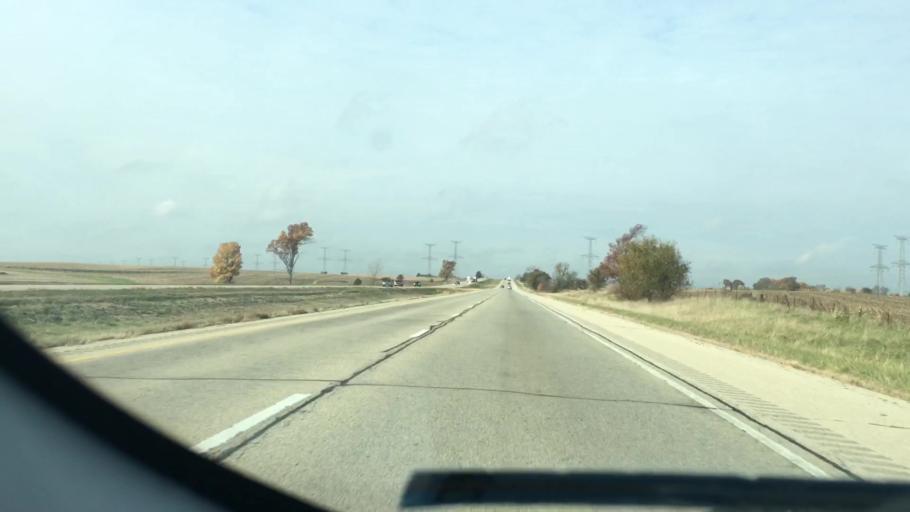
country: US
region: Illinois
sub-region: Tazewell County
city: Morton
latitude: 40.6225
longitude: -89.3762
